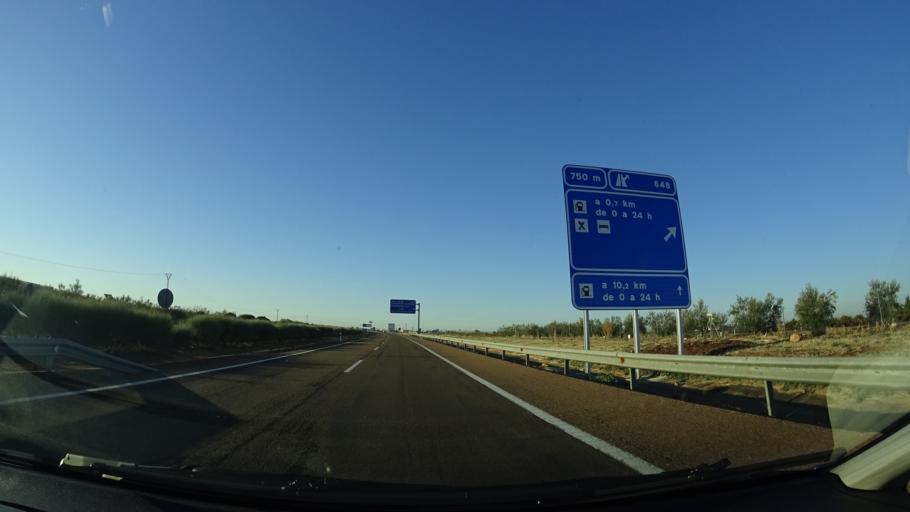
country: ES
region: Extremadura
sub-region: Provincia de Badajoz
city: Almendralejo
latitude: 38.7205
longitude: -6.3959
